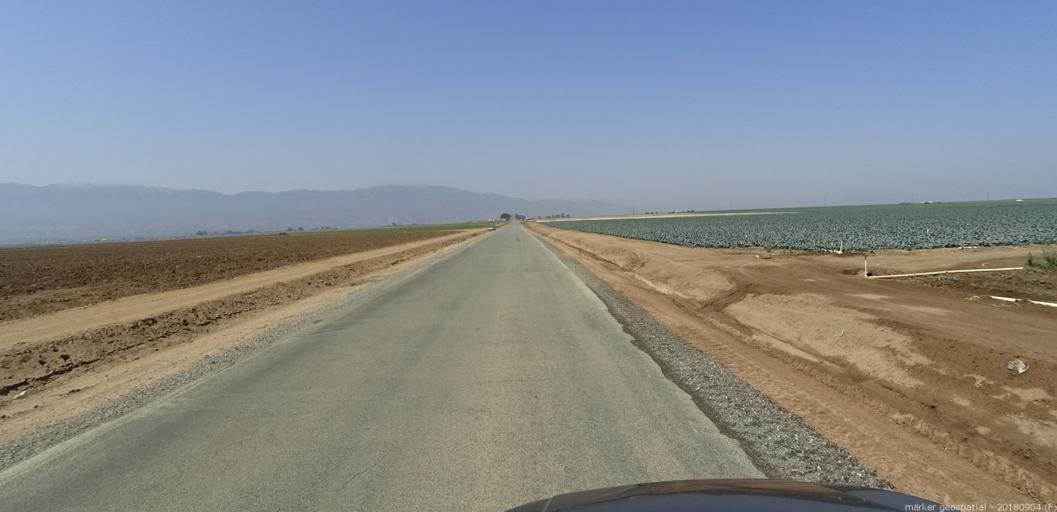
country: US
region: California
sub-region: Monterey County
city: Gonzales
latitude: 36.5580
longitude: -121.4512
